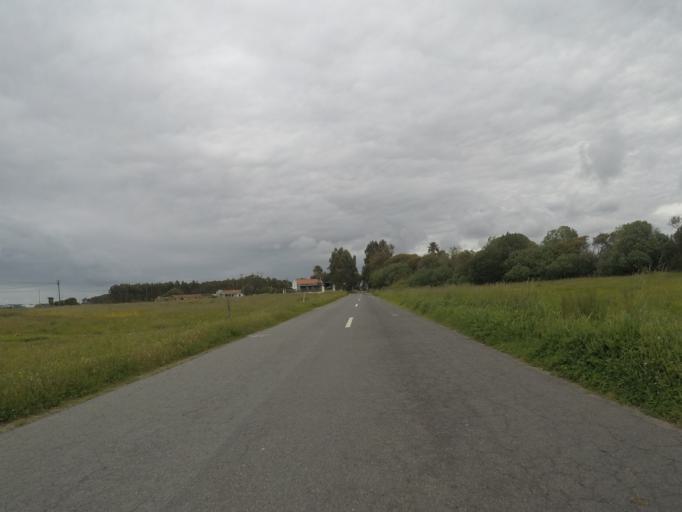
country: PT
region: Beja
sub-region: Odemira
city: Sao Teotonio
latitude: 37.5910
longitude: -8.7776
